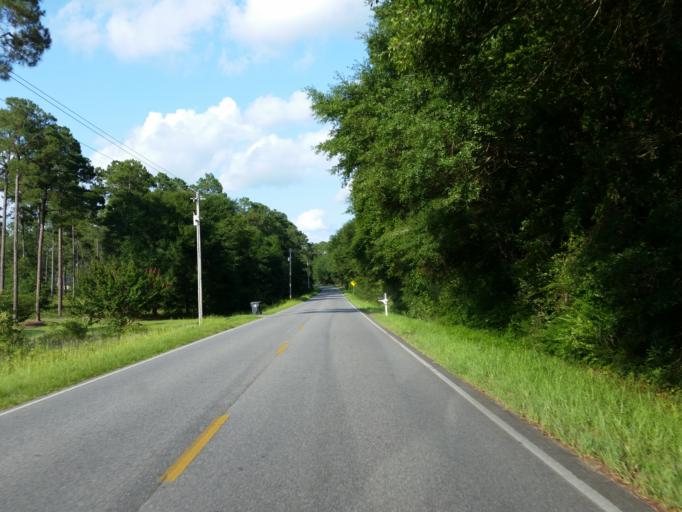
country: US
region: Georgia
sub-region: Crisp County
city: Cordele
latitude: 31.9649
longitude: -83.8845
